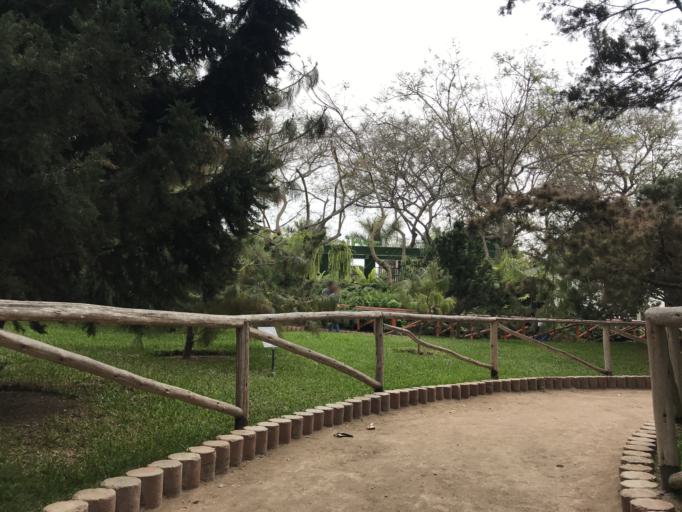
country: PE
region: Callao
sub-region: Callao
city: Callao
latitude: -12.0686
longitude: -77.0873
